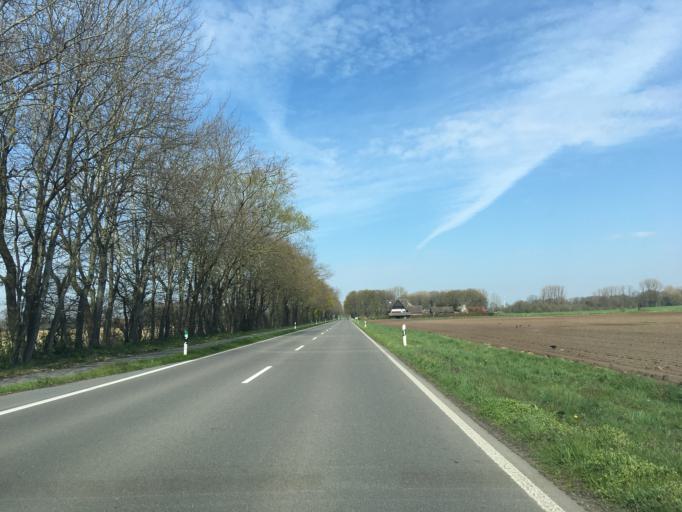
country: DE
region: North Rhine-Westphalia
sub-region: Regierungsbezirk Munster
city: Vreden
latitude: 52.0124
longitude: 6.8537
